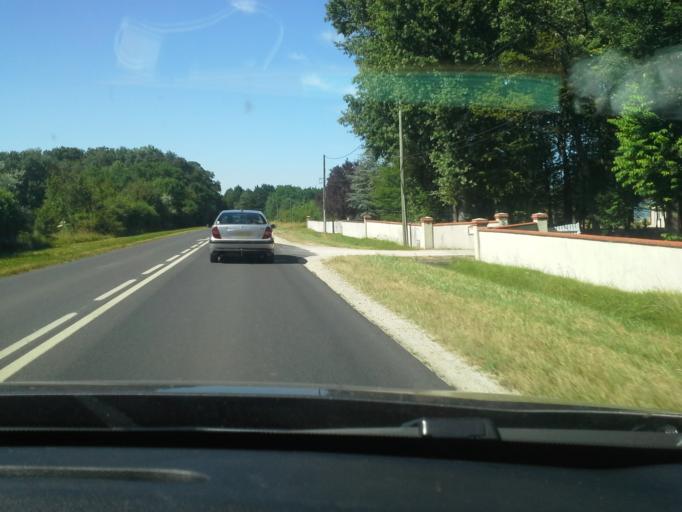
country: FR
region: Centre
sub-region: Departement du Loir-et-Cher
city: Cormeray
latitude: 47.4986
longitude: 1.4056
